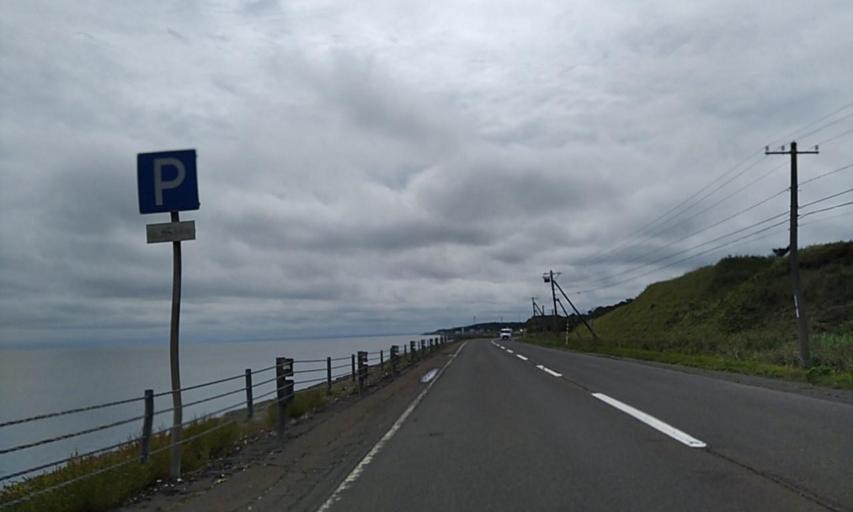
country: JP
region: Hokkaido
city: Shibetsu
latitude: 43.4969
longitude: 145.2476
